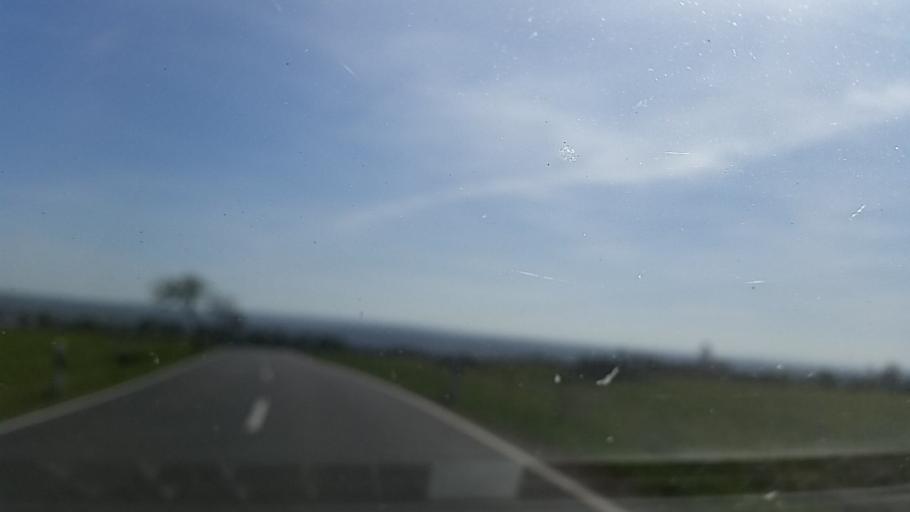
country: DE
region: Lower Saxony
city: Schoningen
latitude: 52.1452
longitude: 10.9427
